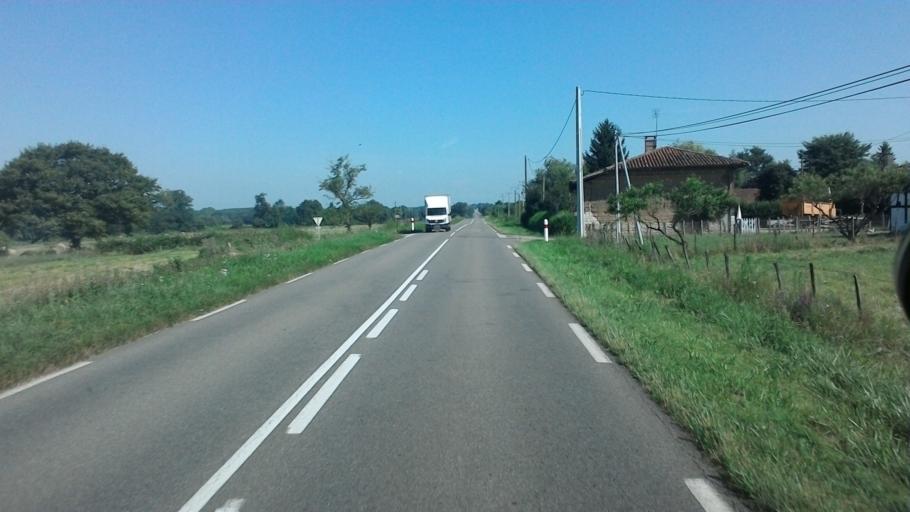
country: FR
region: Rhone-Alpes
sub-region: Departement de l'Ain
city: Saint-Trivier-de-Courtes
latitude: 46.4096
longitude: 5.1058
